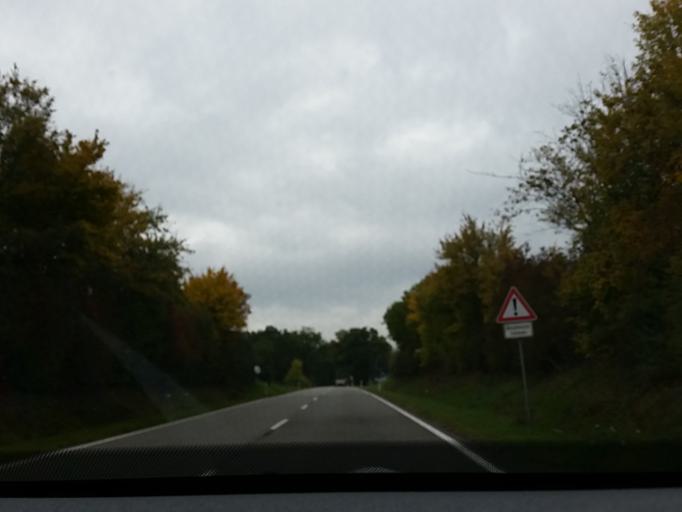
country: DE
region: Saarland
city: Weiskirchen
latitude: 49.5017
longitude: 6.8319
